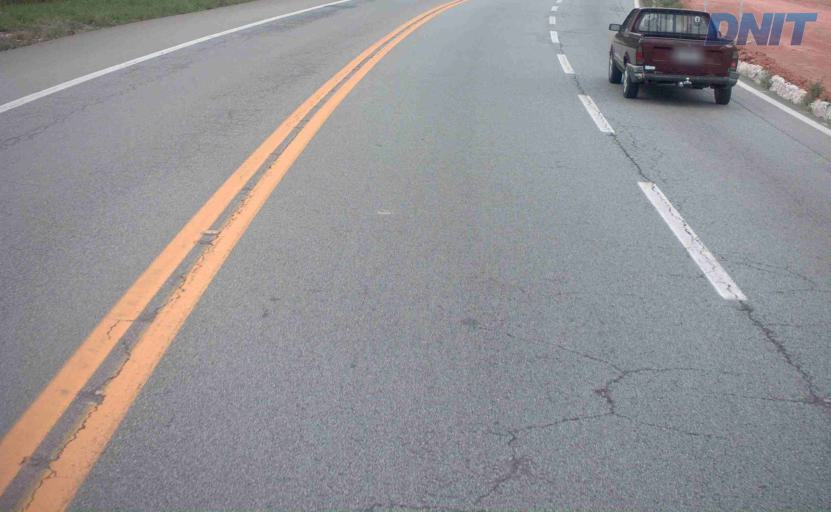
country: BR
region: Minas Gerais
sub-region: Barao De Cocais
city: Barao de Cocais
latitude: -19.7578
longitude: -43.4708
